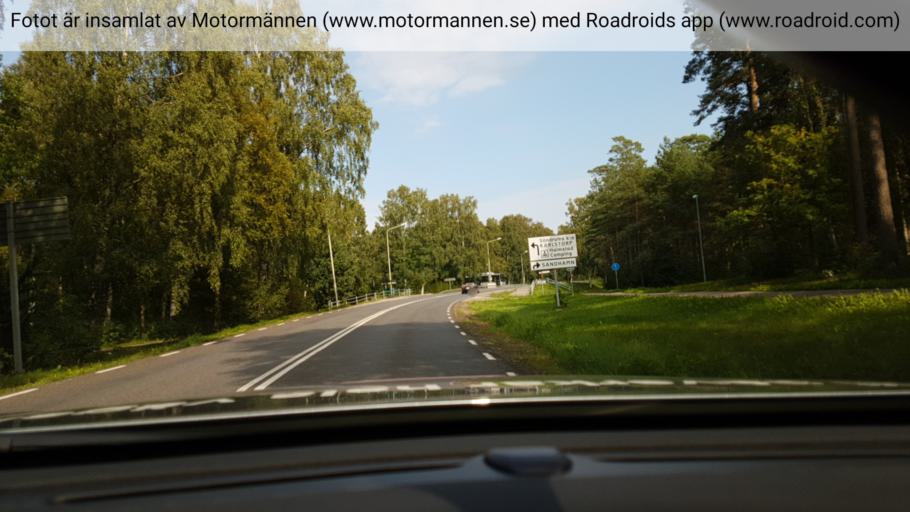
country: SE
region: Halland
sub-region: Halmstads Kommun
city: Mjallby
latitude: 56.6557
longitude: 12.7548
